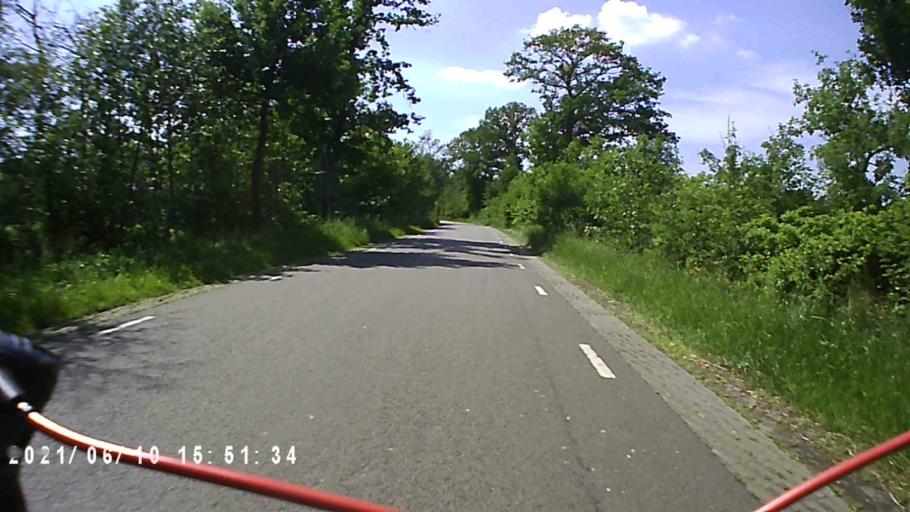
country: NL
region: Friesland
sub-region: Gemeente Achtkarspelen
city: Harkema
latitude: 53.1729
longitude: 6.1171
